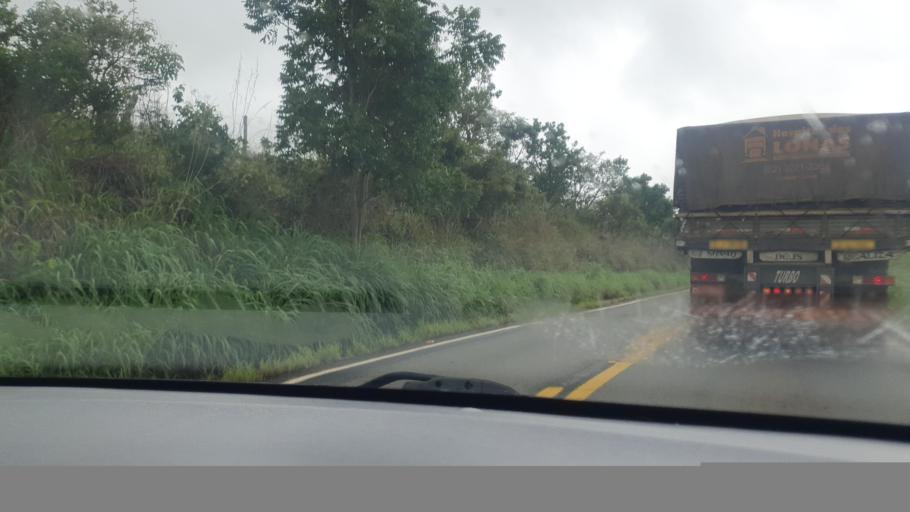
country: BR
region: Goias
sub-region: Vianopolis
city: Vianopolis
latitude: -16.9502
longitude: -48.5964
